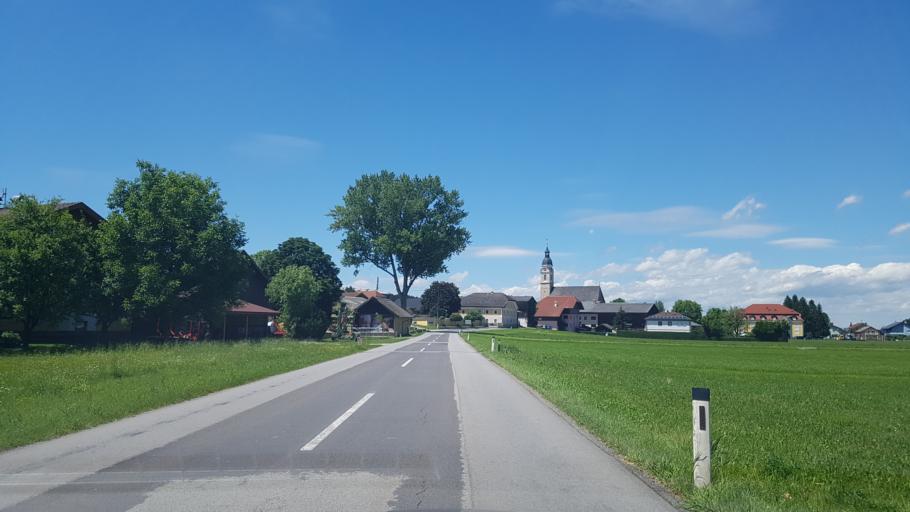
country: AT
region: Salzburg
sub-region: Politischer Bezirk Salzburg-Umgebung
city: Strasswalchen
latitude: 48.0030
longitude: 13.2211
